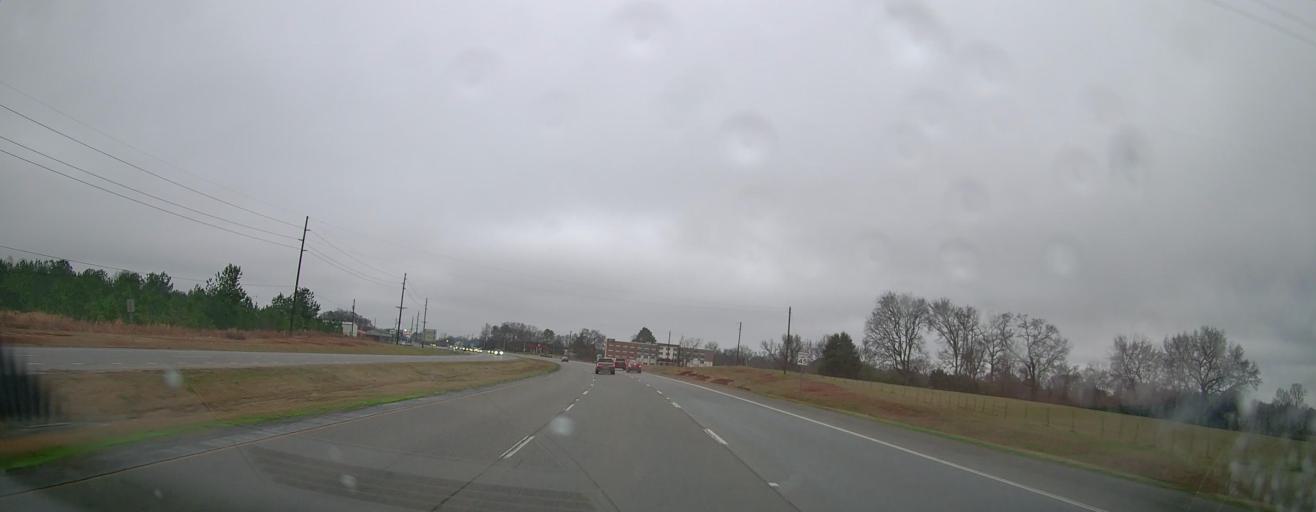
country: US
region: Alabama
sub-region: Morgan County
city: Decatur
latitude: 34.5950
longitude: -87.0315
